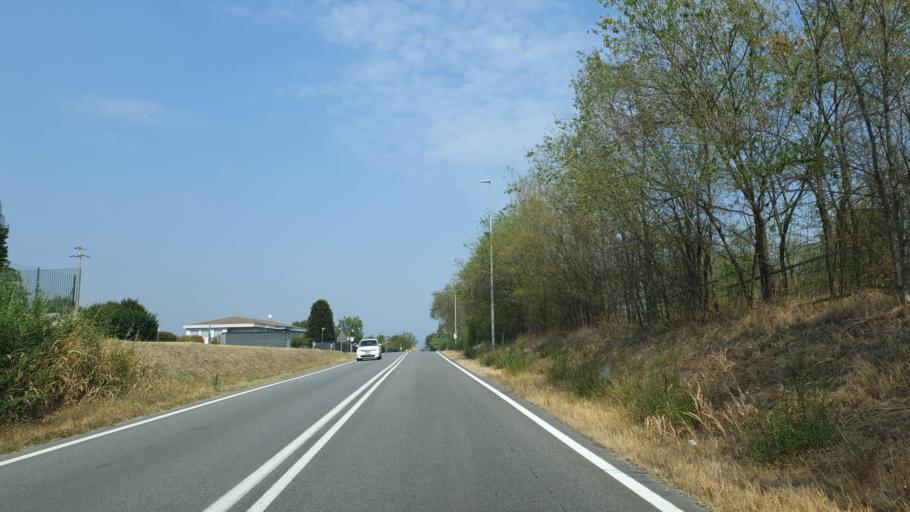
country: IT
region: Lombardy
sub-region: Provincia di Brescia
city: Montirone
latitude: 45.4306
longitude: 10.2579
